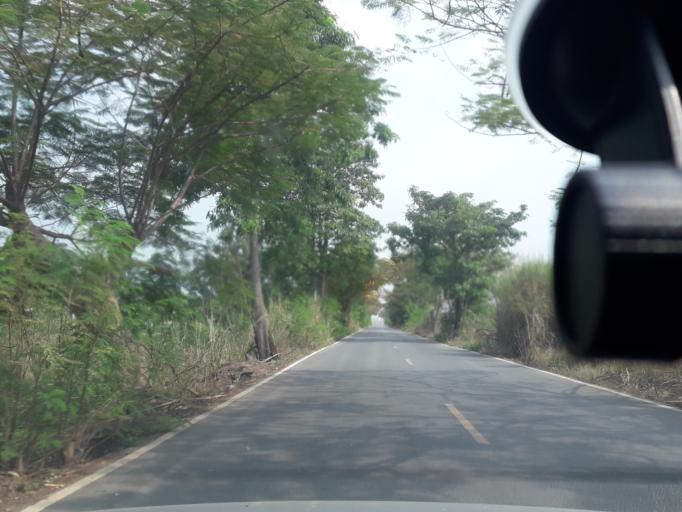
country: TH
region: Pathum Thani
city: Nong Suea
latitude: 14.1967
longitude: 100.8877
